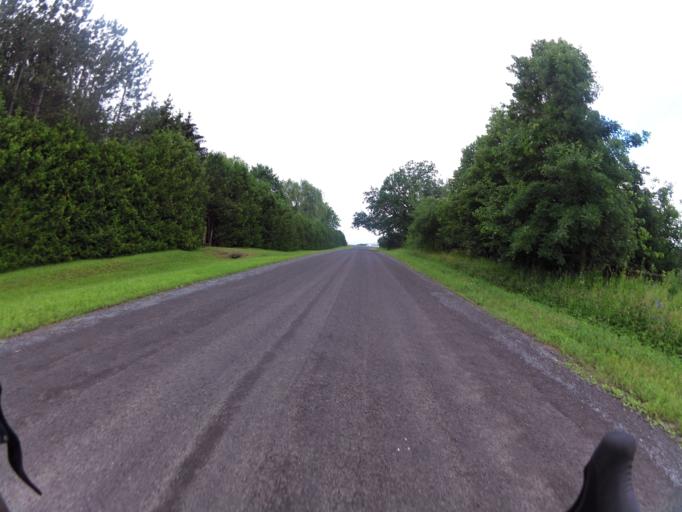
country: CA
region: Ontario
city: Bells Corners
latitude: 45.2542
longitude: -75.8732
